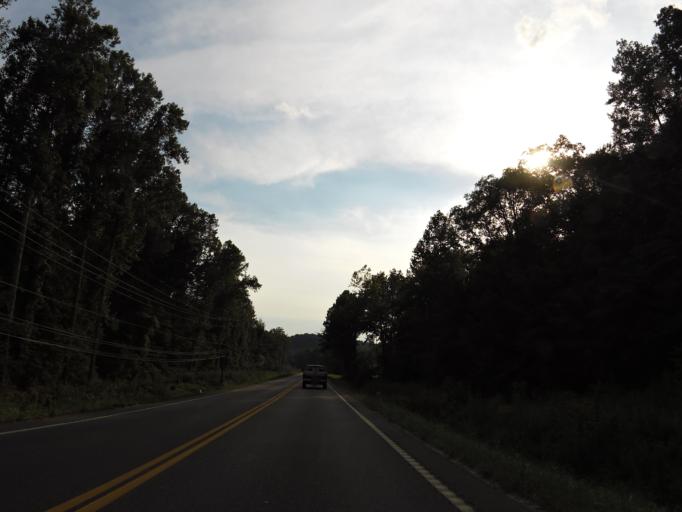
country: US
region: Tennessee
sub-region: Roane County
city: Oliver Springs
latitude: 36.0483
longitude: -84.3571
